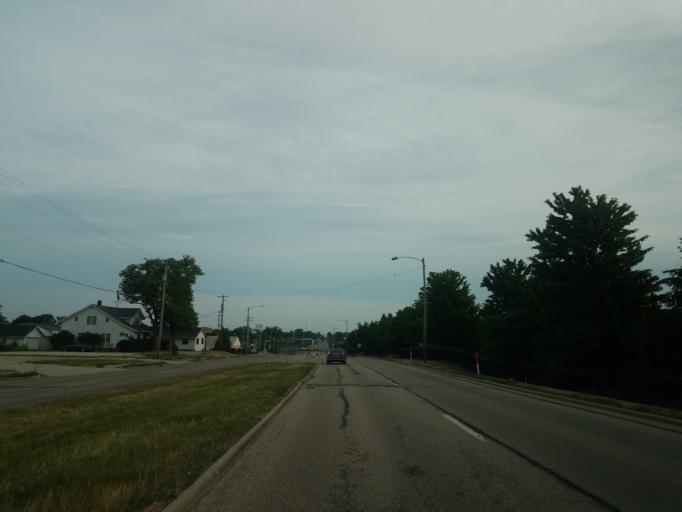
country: US
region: Illinois
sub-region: McLean County
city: Bloomington
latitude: 40.4544
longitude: -88.9925
